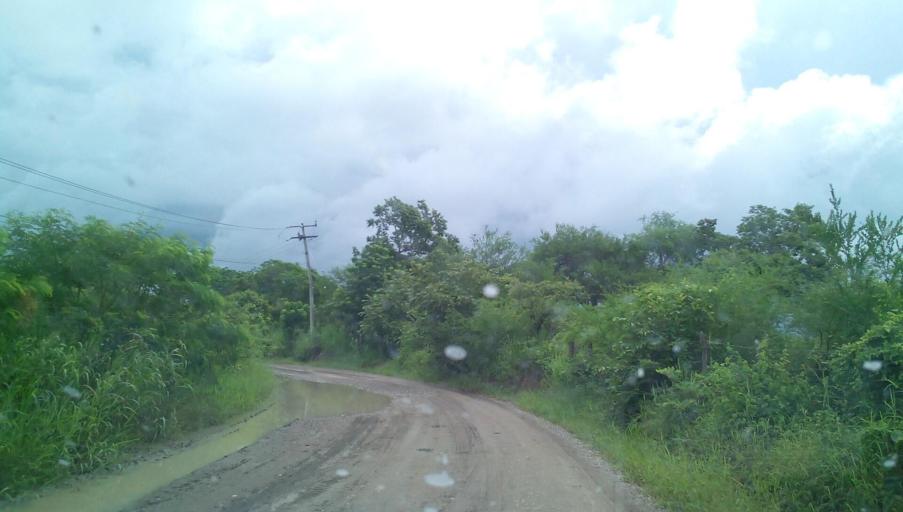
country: MX
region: Veracruz
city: Panuco
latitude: 21.8428
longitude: -98.1363
